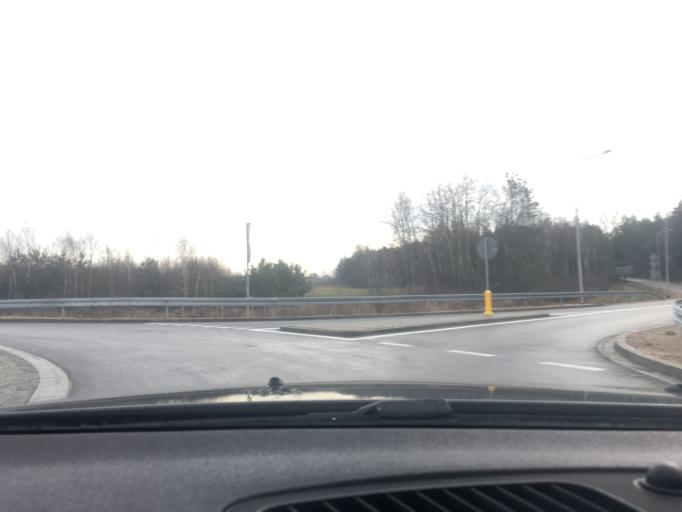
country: PL
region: Swietokrzyskie
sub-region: Powiat jedrzejowski
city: Sobkow
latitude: 50.6880
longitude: 20.3717
